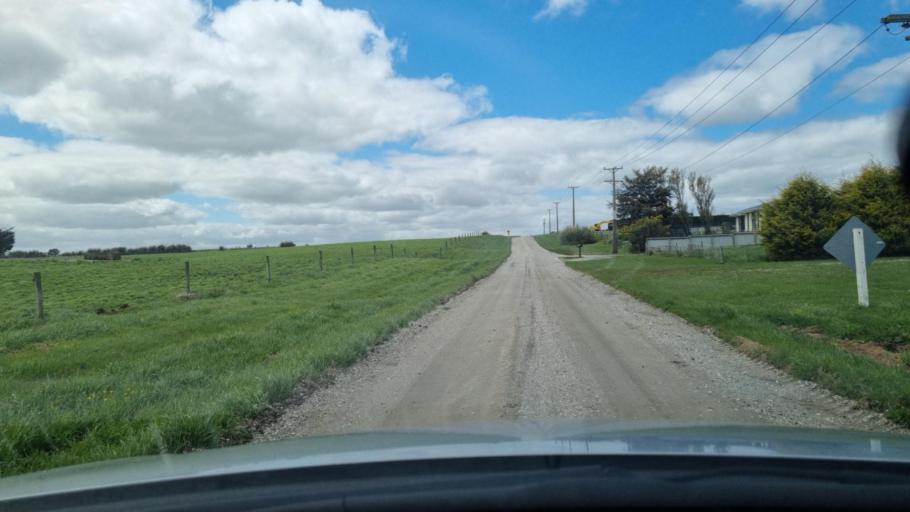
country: NZ
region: Southland
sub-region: Invercargill City
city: Invercargill
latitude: -46.4506
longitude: 168.4139
